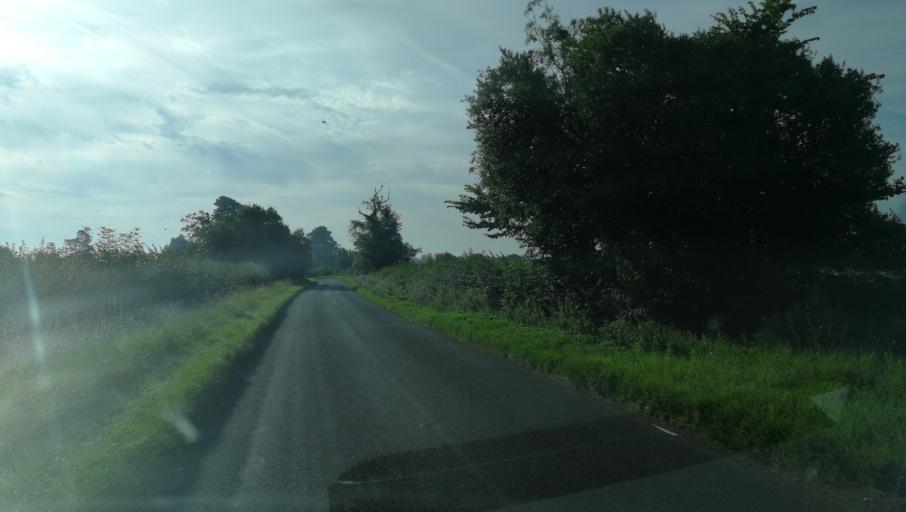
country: GB
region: England
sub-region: Oxfordshire
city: Bloxham
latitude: 52.0242
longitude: -1.3947
